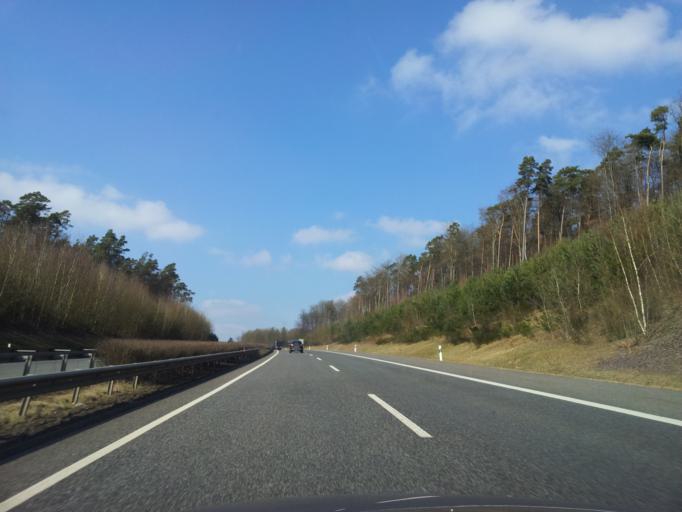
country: DE
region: Rheinland-Pfalz
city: Bergweiler
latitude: 49.9772
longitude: 6.8207
